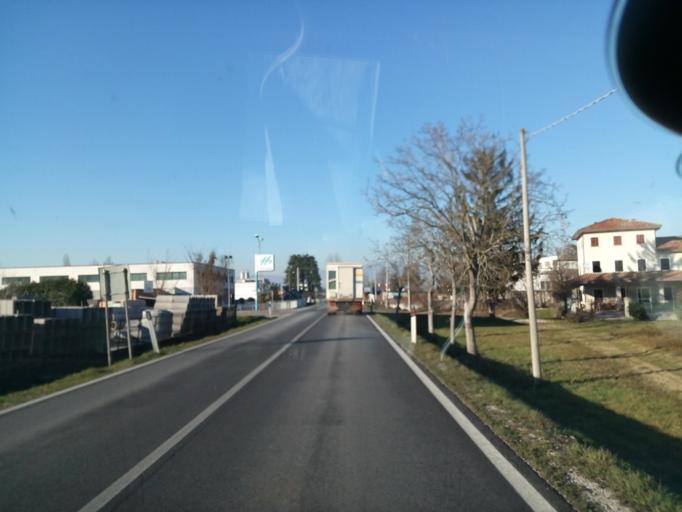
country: IT
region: Veneto
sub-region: Provincia di Treviso
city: Resana
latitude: 45.6474
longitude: 11.9467
